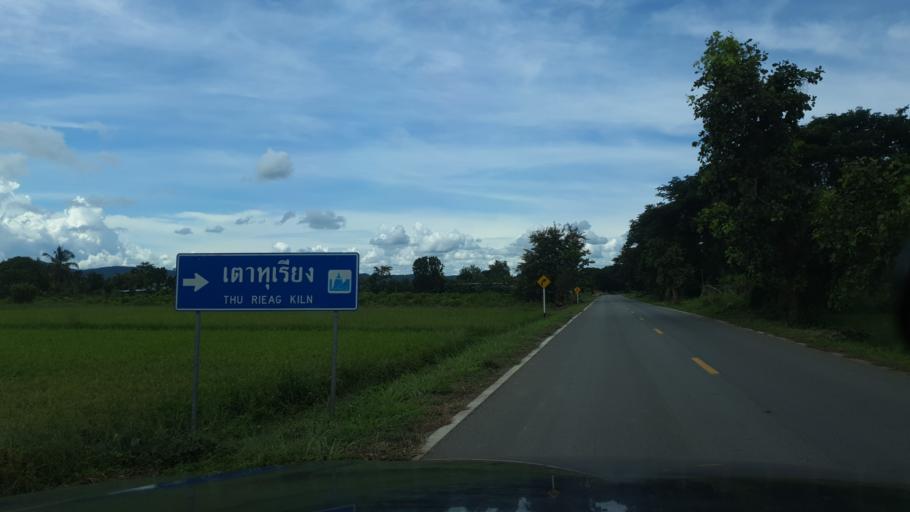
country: TH
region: Sukhothai
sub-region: Amphoe Si Satchanalai
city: Si Satchanalai
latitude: 17.4732
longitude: 99.7544
